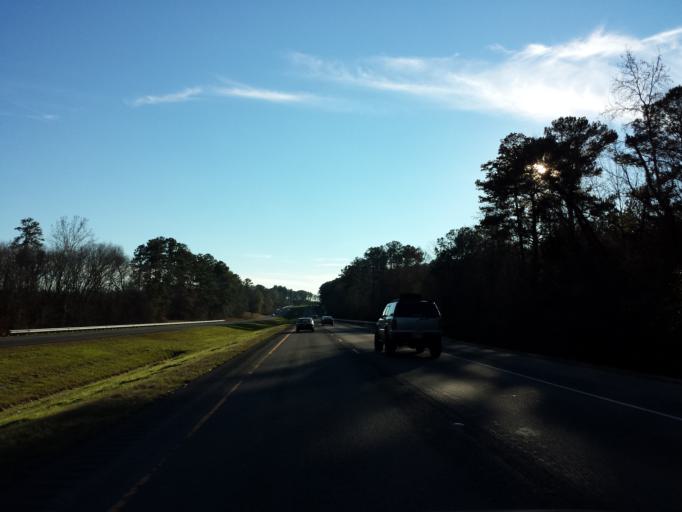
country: US
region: Alabama
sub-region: Greene County
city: Eutaw
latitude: 32.8860
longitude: -87.9056
